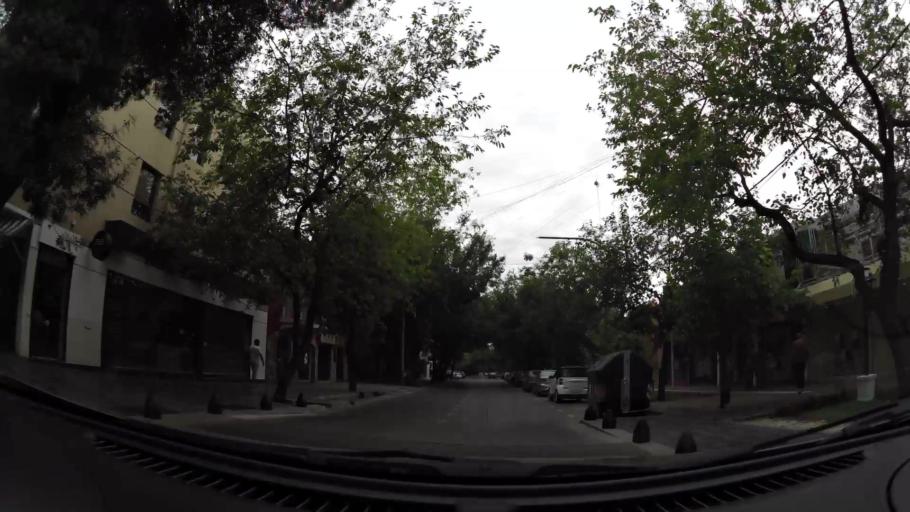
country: AR
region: Mendoza
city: Mendoza
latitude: -32.8913
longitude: -68.8590
